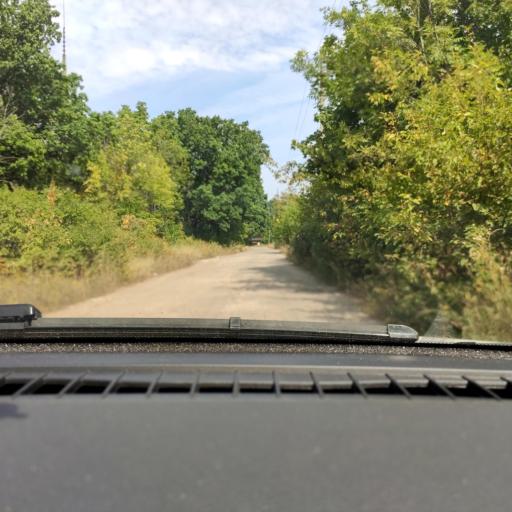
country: RU
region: Voronezj
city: Pridonskoy
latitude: 51.7555
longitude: 39.0789
